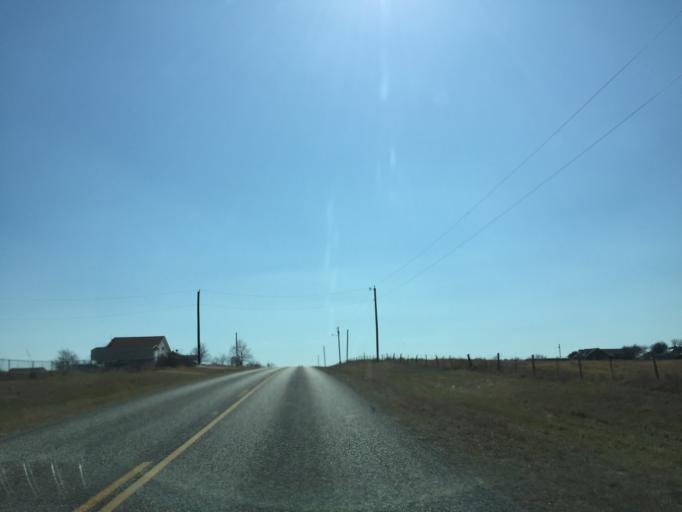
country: US
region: Texas
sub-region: Williamson County
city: Serenada
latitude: 30.7242
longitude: -97.5829
